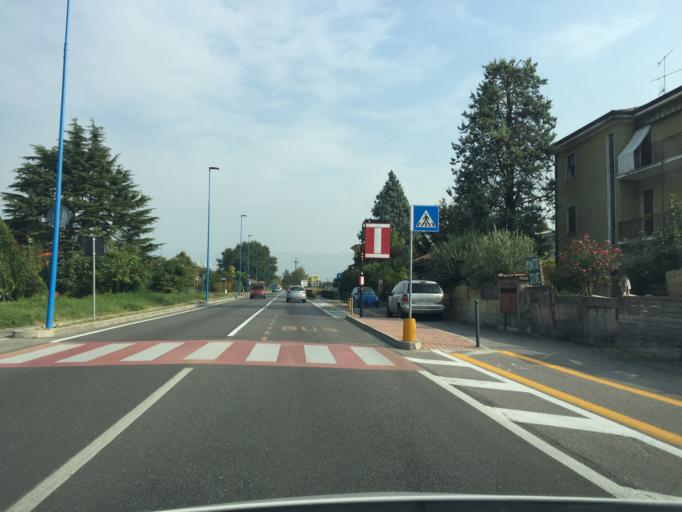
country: IT
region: Lombardy
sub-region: Provincia di Brescia
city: Folzano
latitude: 45.5061
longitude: 10.1909
